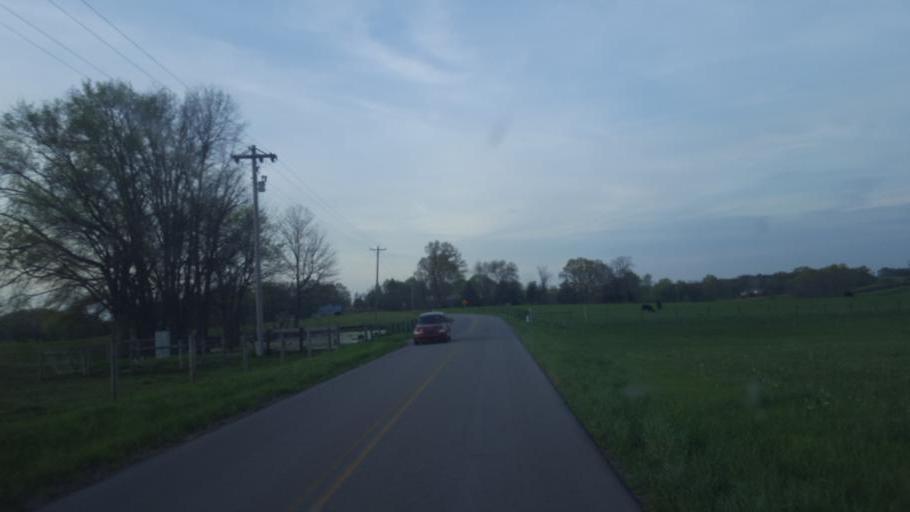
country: US
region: Kentucky
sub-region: Metcalfe County
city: Edmonton
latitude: 37.0740
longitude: -85.7068
